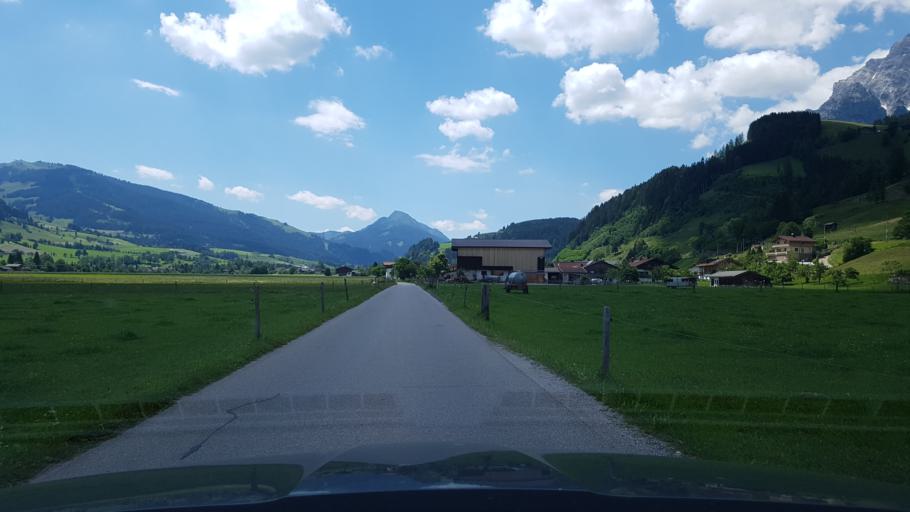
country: AT
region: Salzburg
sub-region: Politischer Bezirk Zell am See
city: Leogang
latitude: 47.4444
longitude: 12.7939
